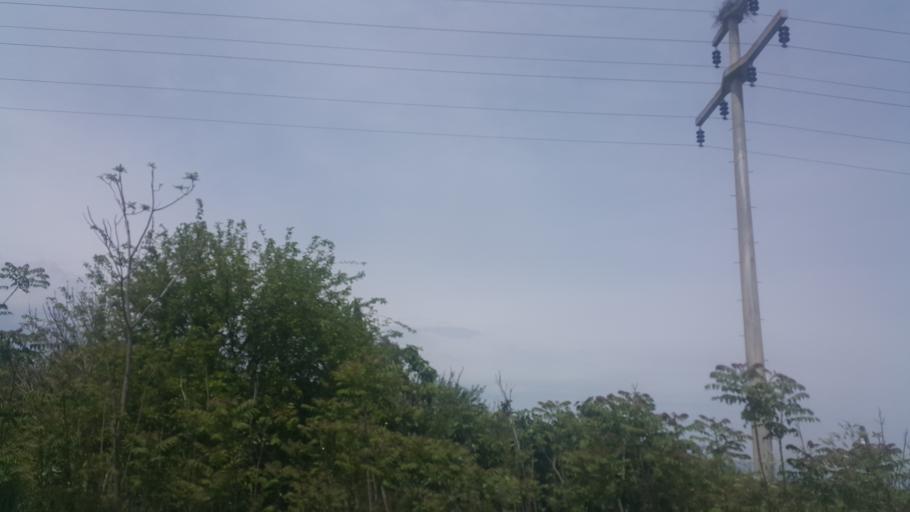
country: TR
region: Adana
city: Kosreli
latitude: 37.0654
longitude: 35.9657
